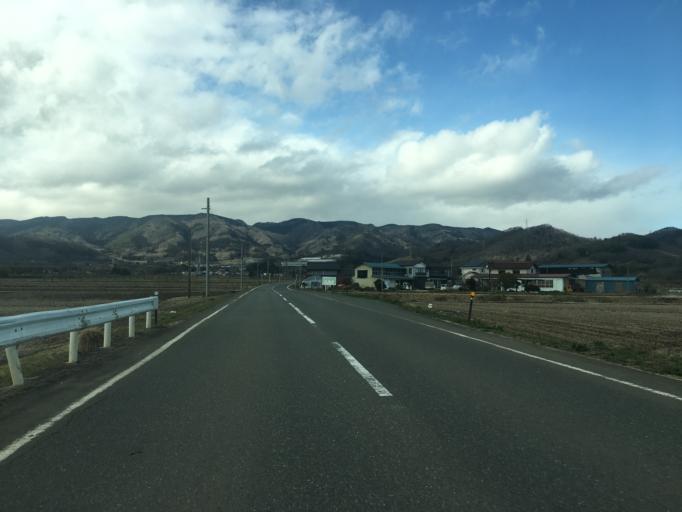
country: JP
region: Fukushima
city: Yanagawamachi-saiwaicho
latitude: 37.8806
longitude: 140.5932
